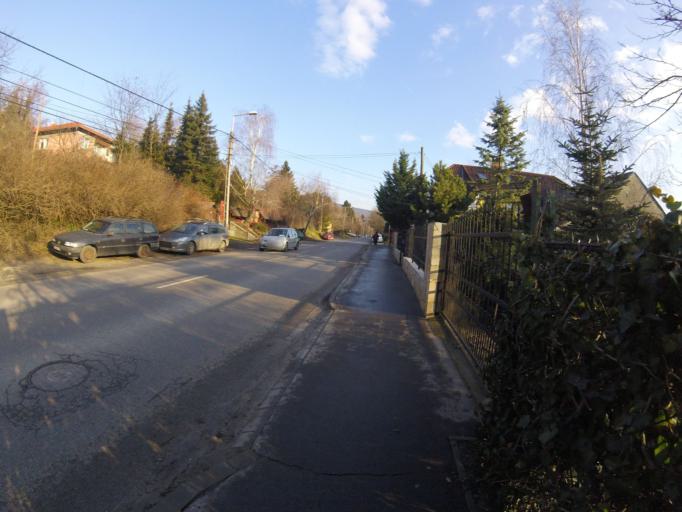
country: HU
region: Pest
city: Budakeszi
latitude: 47.5473
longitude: 18.9562
